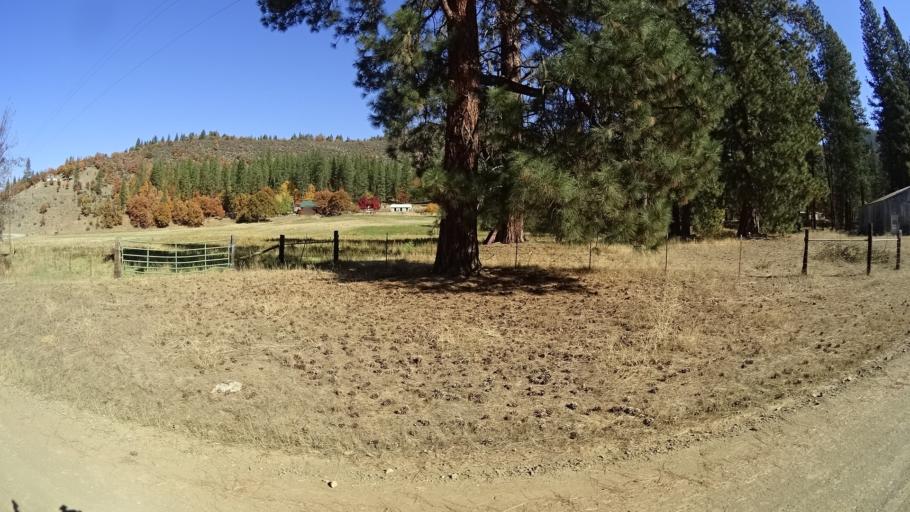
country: US
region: California
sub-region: Siskiyou County
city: Yreka
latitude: 41.6032
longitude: -122.9594
